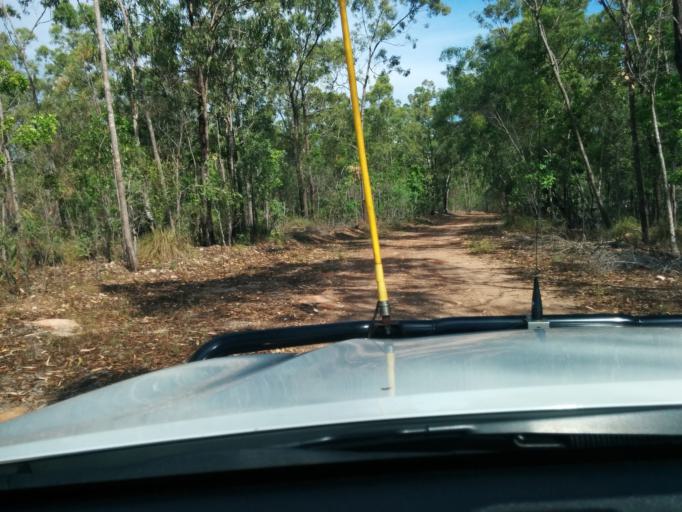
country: AU
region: Northern Territory
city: Alyangula
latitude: -13.8432
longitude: 136.4177
